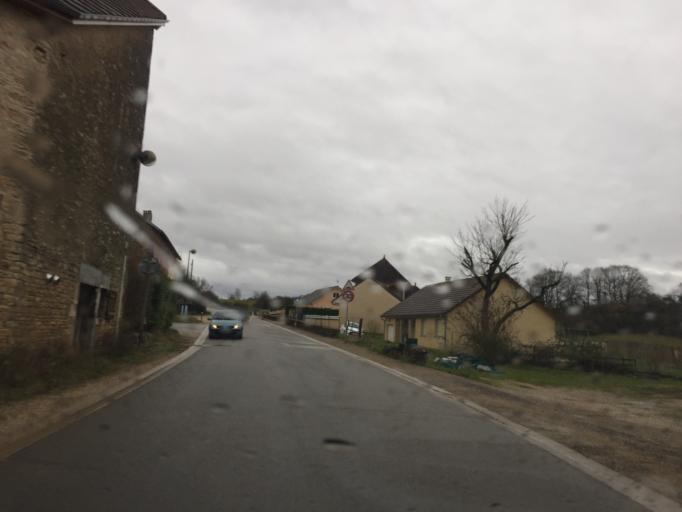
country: FR
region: Franche-Comte
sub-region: Departement du Jura
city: Dole
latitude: 47.1626
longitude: 5.5646
